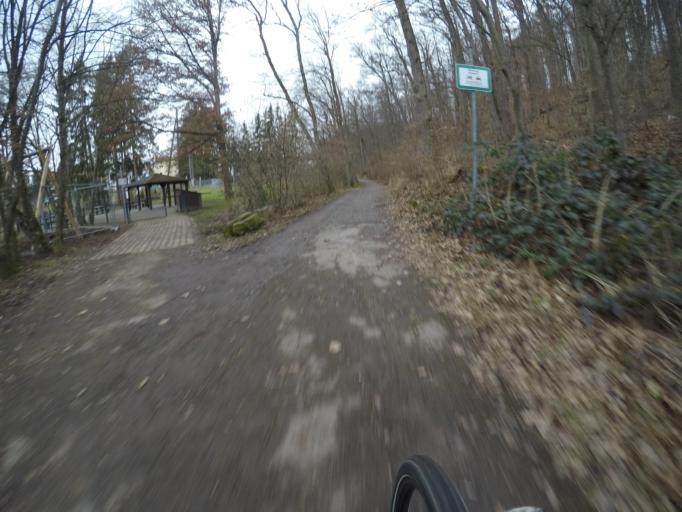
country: DE
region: Baden-Wuerttemberg
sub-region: Regierungsbezirk Stuttgart
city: Sindelfingen
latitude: 48.7080
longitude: 9.0402
